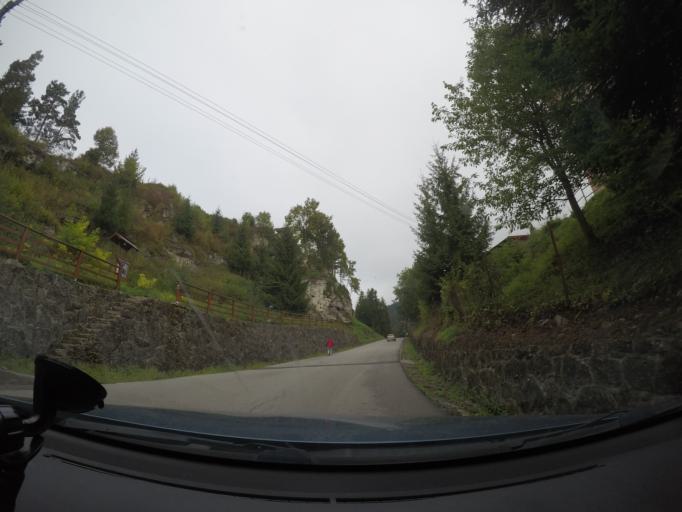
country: SK
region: Zilinsky
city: Ruzomberok
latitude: 49.1297
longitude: 19.4008
